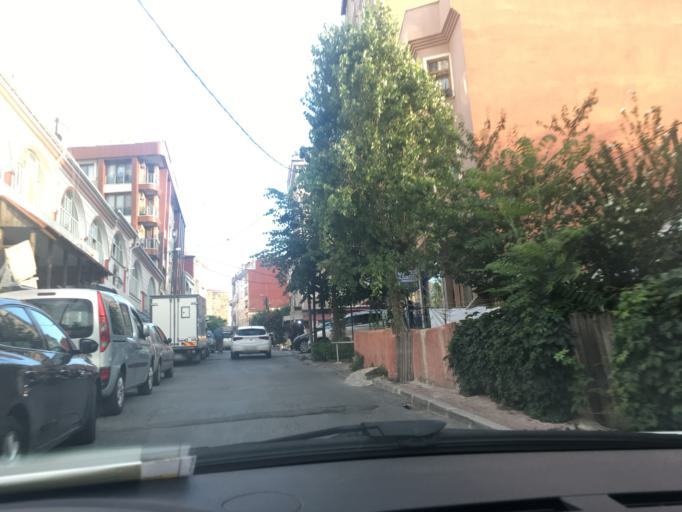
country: TR
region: Istanbul
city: Sisli
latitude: 41.0556
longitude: 28.9743
